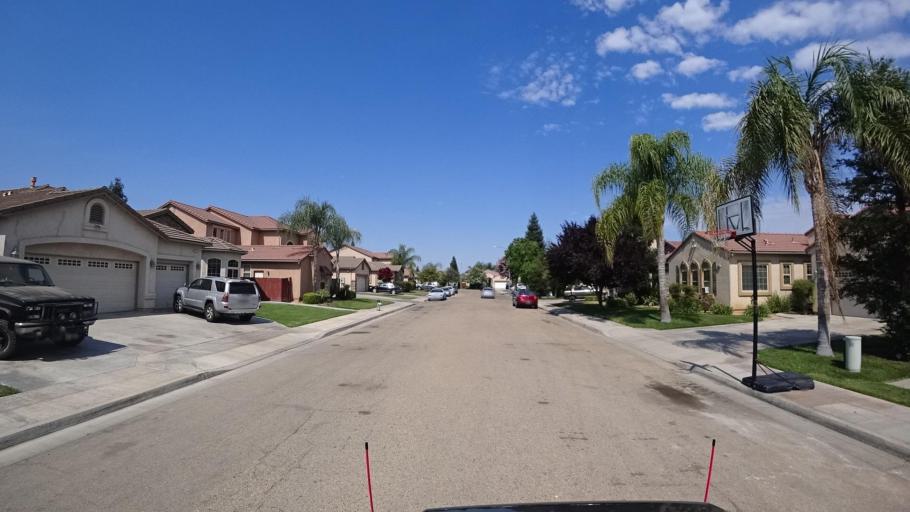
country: US
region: California
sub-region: Fresno County
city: Sunnyside
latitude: 36.7197
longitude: -119.6872
